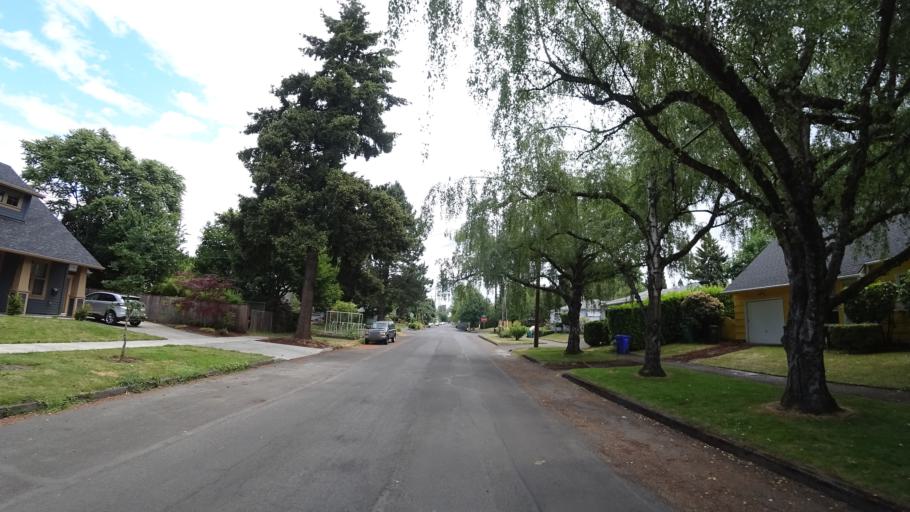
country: US
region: Oregon
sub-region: Washington County
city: West Haven
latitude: 45.5807
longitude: -122.7317
